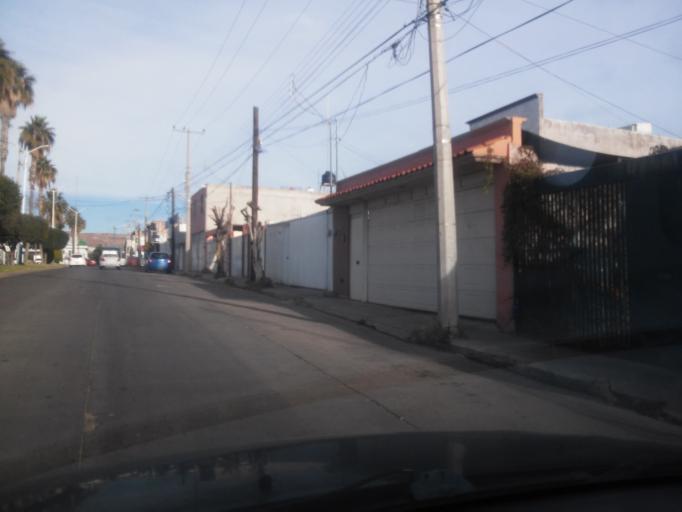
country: MX
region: Durango
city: Victoria de Durango
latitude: 24.0393
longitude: -104.6559
